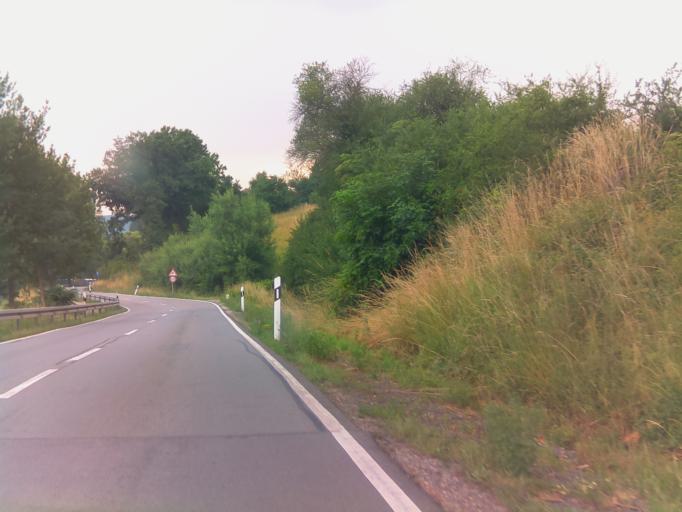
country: DE
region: Hesse
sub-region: Regierungsbezirk Darmstadt
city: Rimbach
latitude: 49.6434
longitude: 8.7661
